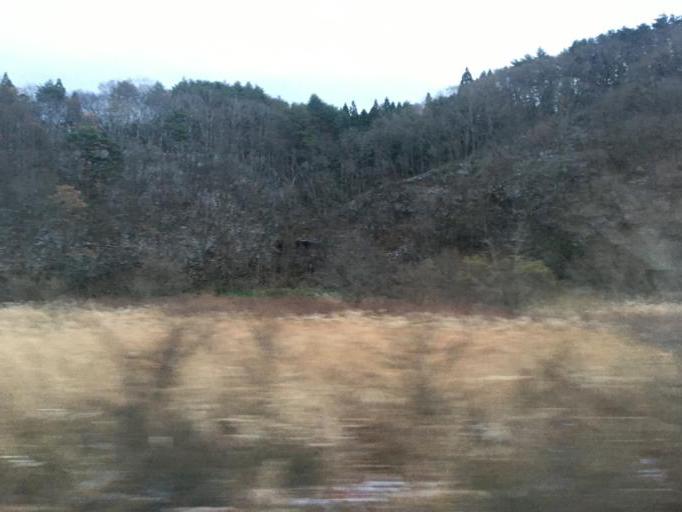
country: JP
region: Aomori
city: Aomori Shi
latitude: 40.8158
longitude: 140.6488
